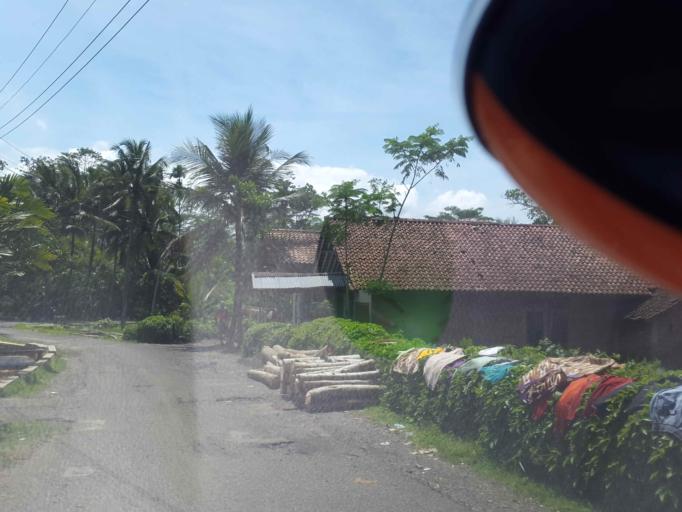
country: ID
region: Central Java
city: Wonosobo
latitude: -7.3541
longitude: 109.6761
